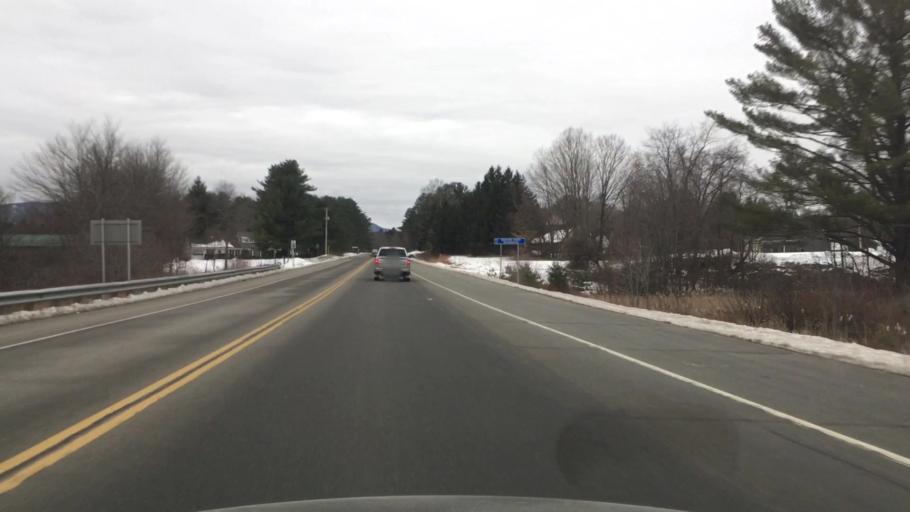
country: US
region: New Hampshire
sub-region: Merrimack County
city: Sutton
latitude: 43.2636
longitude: -71.9509
